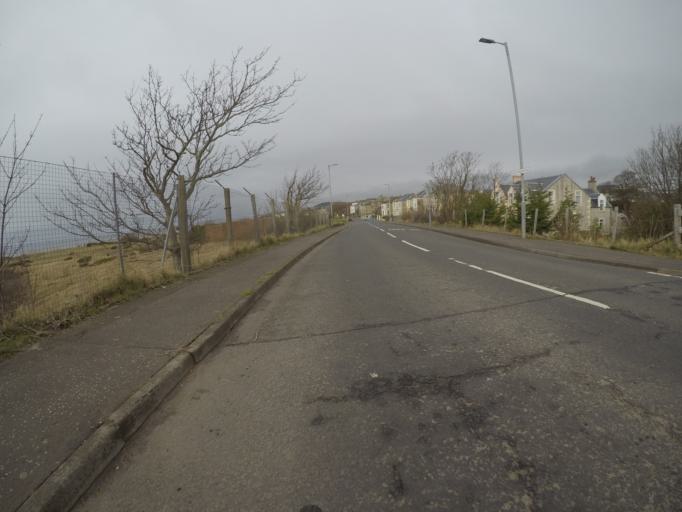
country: GB
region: Scotland
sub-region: North Ayrshire
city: Ardrossan
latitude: 55.6467
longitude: -4.8126
